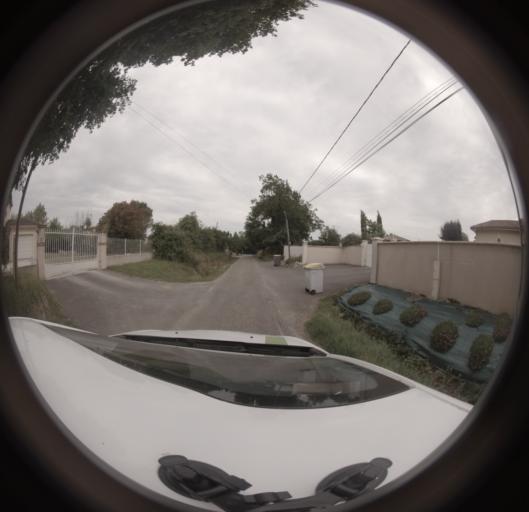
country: FR
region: Midi-Pyrenees
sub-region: Departement du Tarn-et-Garonne
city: Montauban
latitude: 44.0052
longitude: 1.3934
